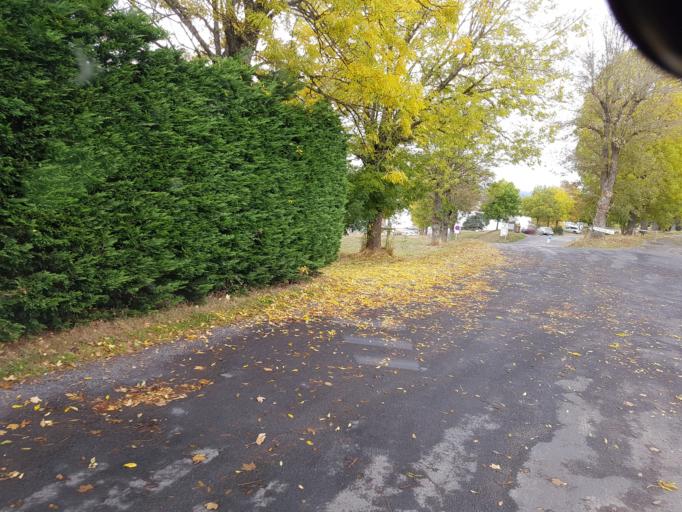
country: FR
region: Languedoc-Roussillon
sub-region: Departement de la Lozere
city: Langogne
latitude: 44.7249
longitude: 3.8395
